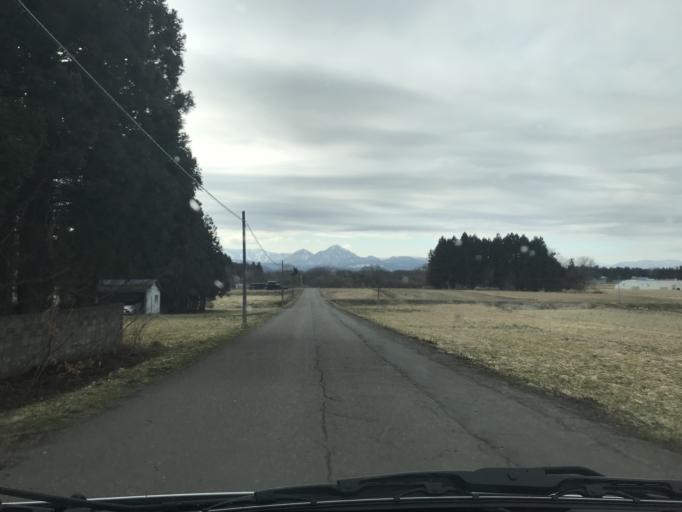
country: JP
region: Iwate
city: Kitakami
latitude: 39.2151
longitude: 141.0594
